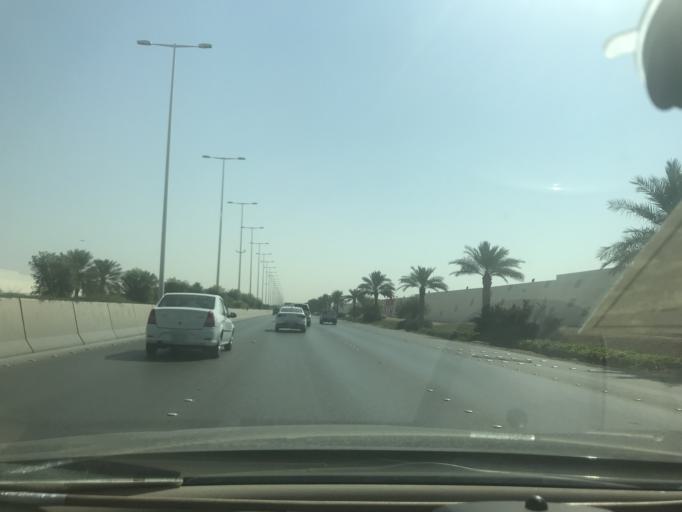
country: SA
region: Ar Riyad
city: Riyadh
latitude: 24.7187
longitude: 46.7141
